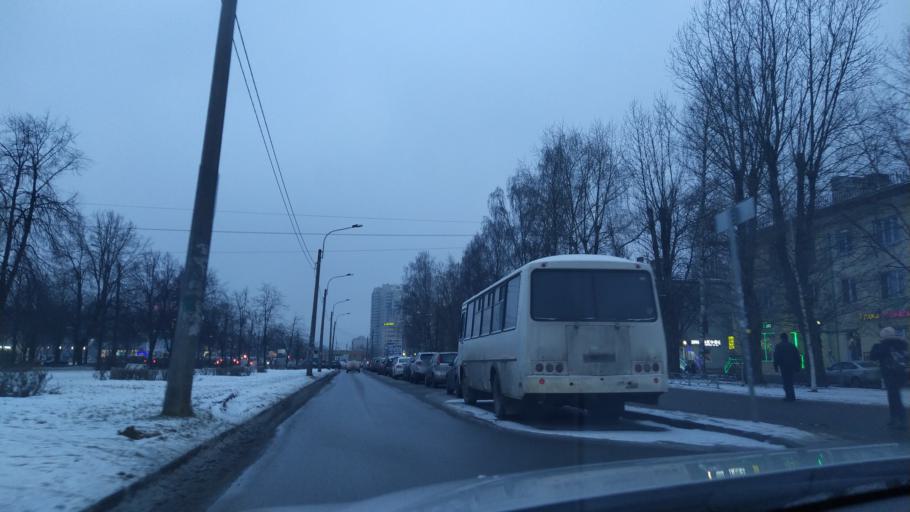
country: RU
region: Leningrad
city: Akademicheskoe
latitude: 60.0155
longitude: 30.3996
